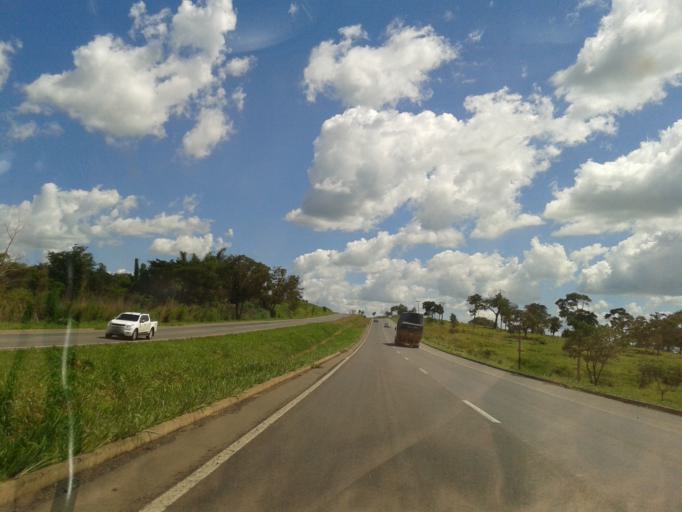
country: BR
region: Goias
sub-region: Piracanjuba
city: Piracanjuba
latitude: -17.3564
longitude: -49.2482
